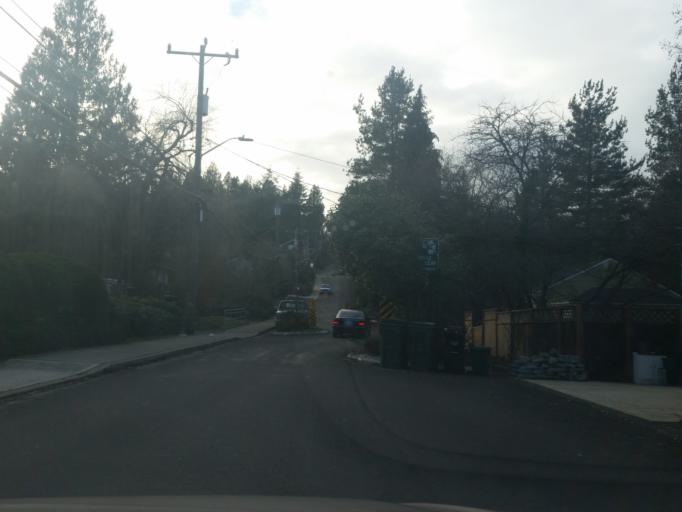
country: US
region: Washington
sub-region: King County
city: Lake Forest Park
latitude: 47.7003
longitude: -122.3043
